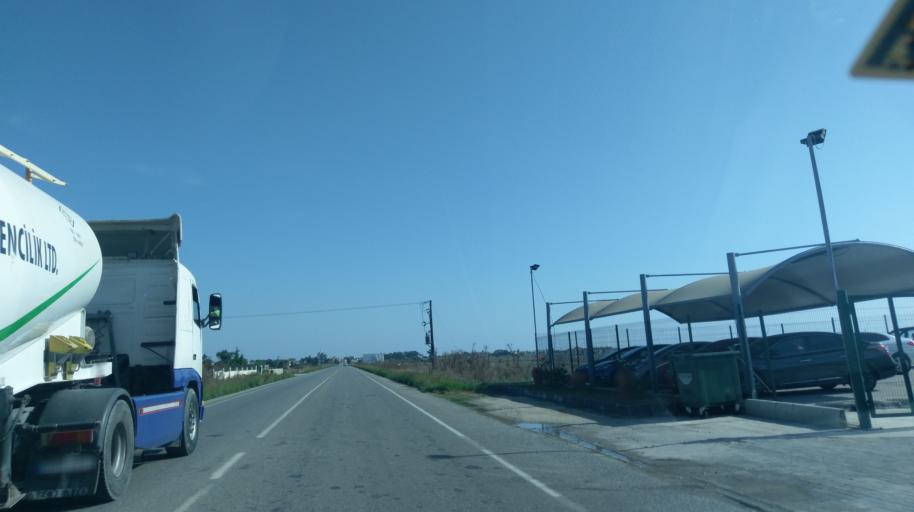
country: CY
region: Ammochostos
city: Trikomo
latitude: 35.2788
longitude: 33.9027
